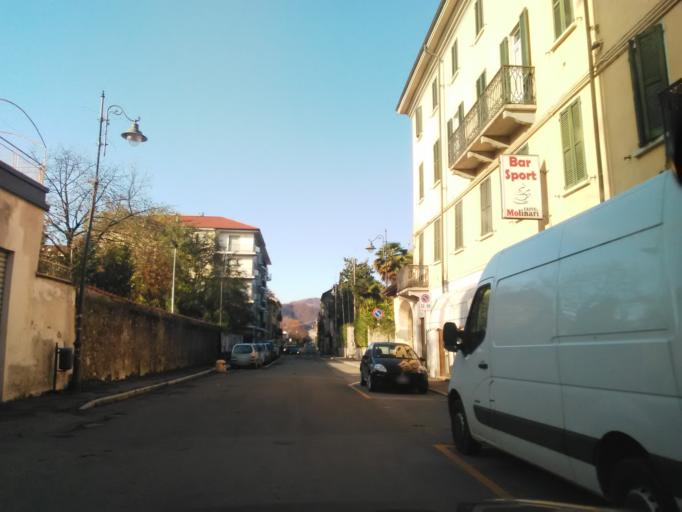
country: IT
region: Piedmont
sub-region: Provincia di Novara
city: Grignasco
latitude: 45.6843
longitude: 8.3367
